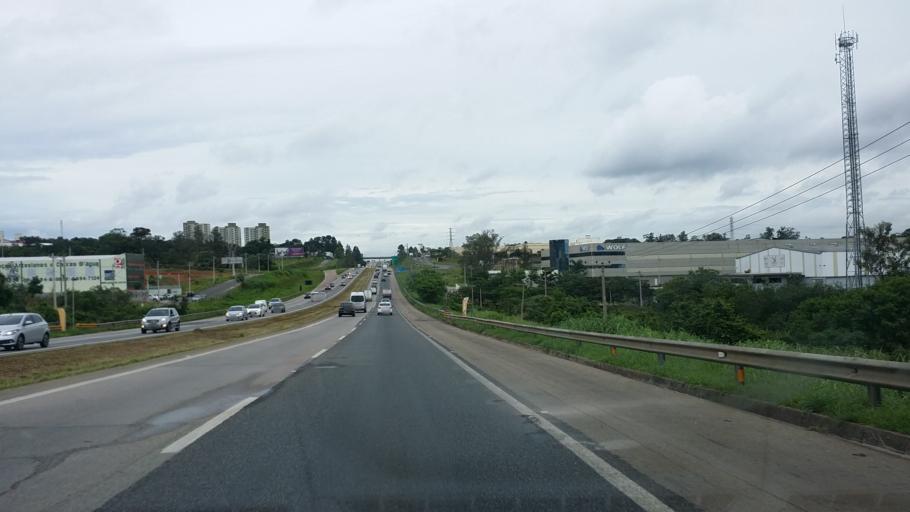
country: BR
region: Sao Paulo
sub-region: Indaiatuba
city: Indaiatuba
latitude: -23.1040
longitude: -47.2003
